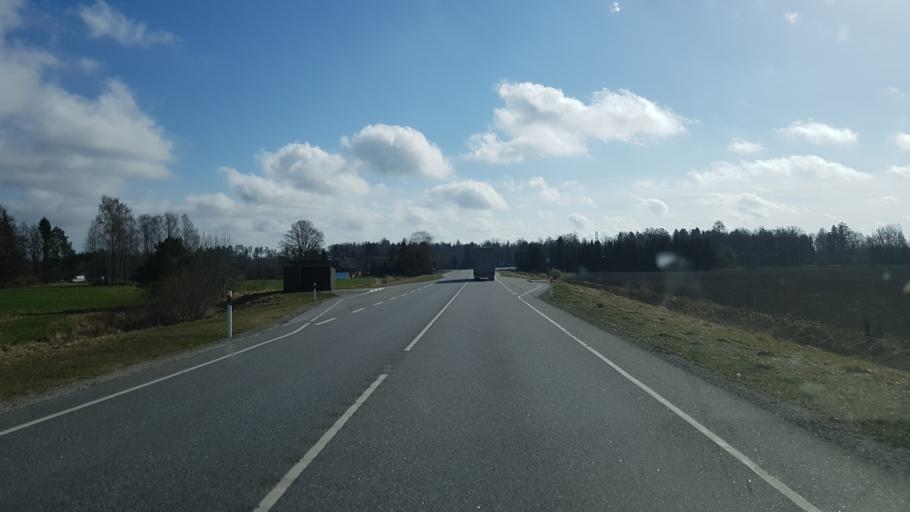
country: EE
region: Paernumaa
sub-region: Vaendra vald (alev)
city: Vandra
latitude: 58.6730
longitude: 25.1107
